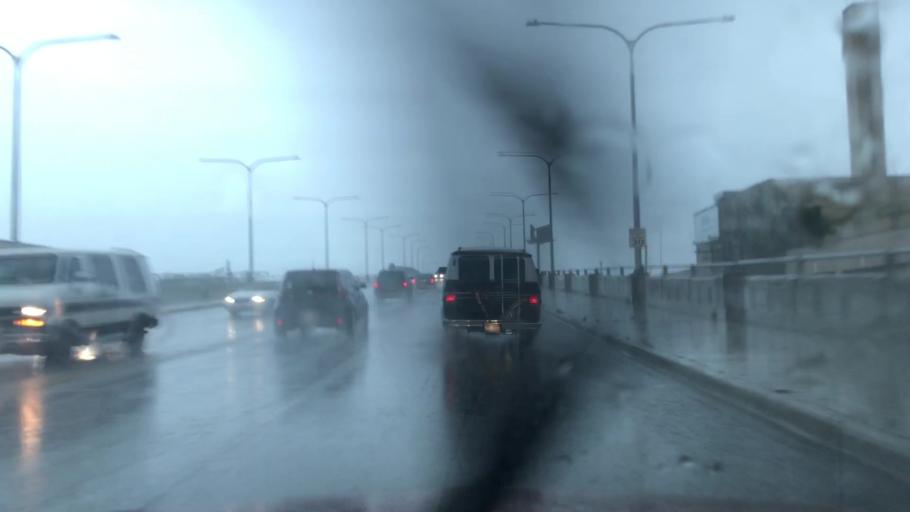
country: US
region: Illinois
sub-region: Cook County
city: Cicero
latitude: 41.8662
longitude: -87.7545
